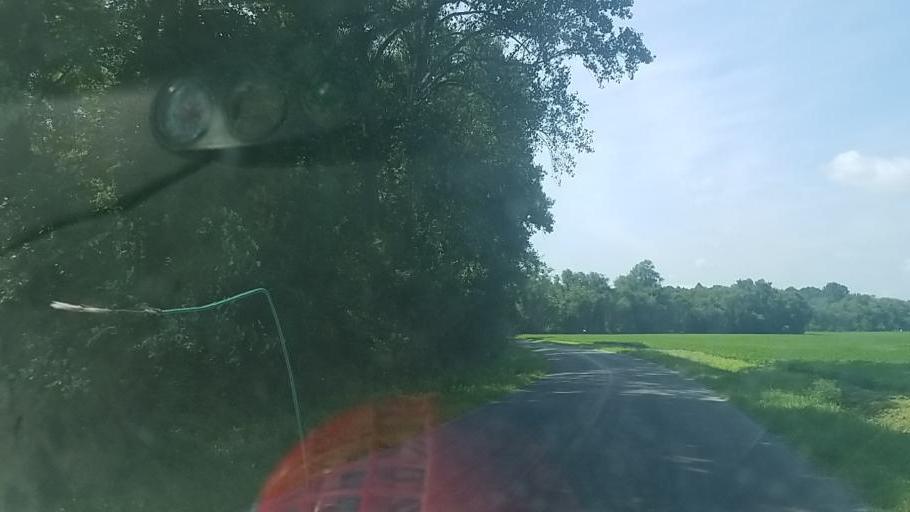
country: US
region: Maryland
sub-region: Caroline County
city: Denton
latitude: 38.8804
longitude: -75.7862
